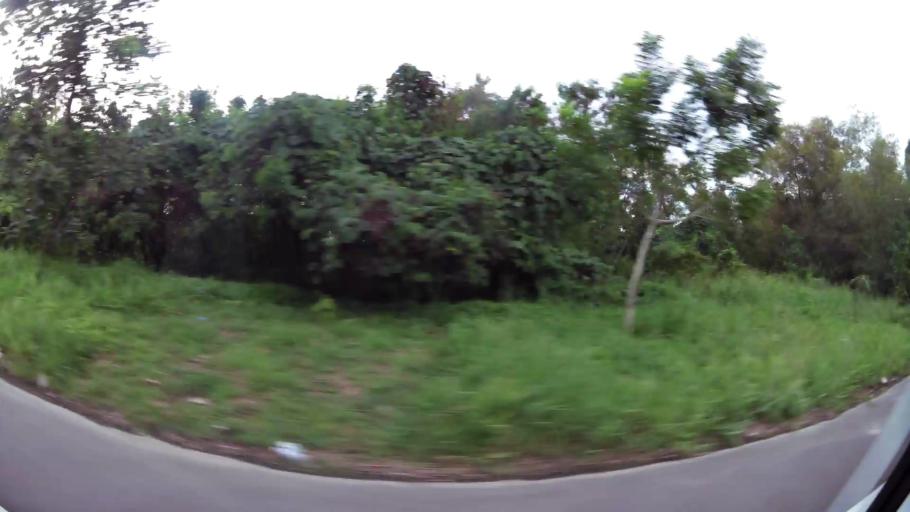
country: BN
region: Brunei and Muara
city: Bandar Seri Begawan
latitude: 4.9983
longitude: 114.9877
